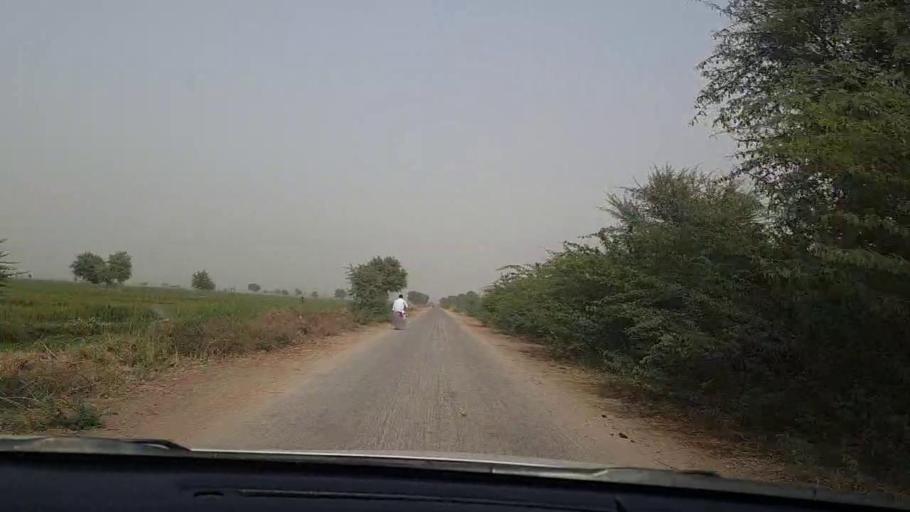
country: PK
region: Sindh
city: Pithoro
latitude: 25.3990
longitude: 69.3811
